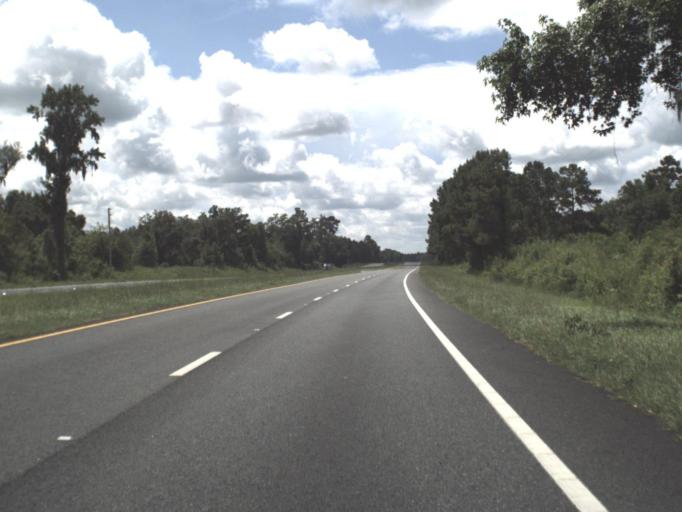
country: US
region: Florida
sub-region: Jefferson County
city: Monticello
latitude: 30.3653
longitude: -83.8027
